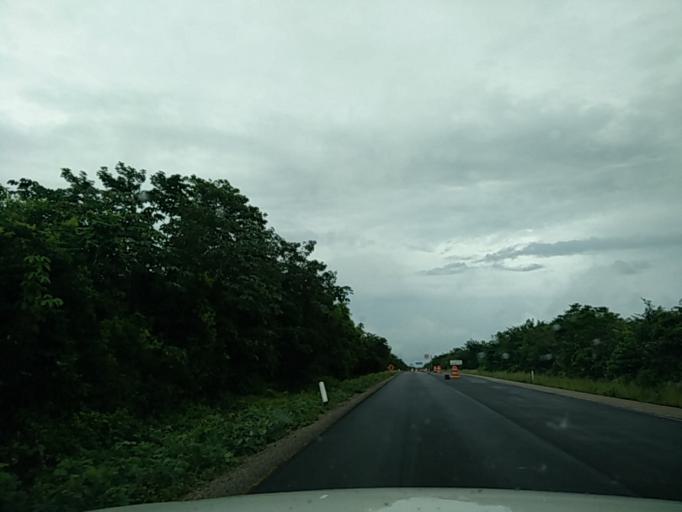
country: MX
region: Quintana Roo
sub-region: Lazaro Cardenas
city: El Tintal
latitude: 20.9014
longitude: -87.4605
